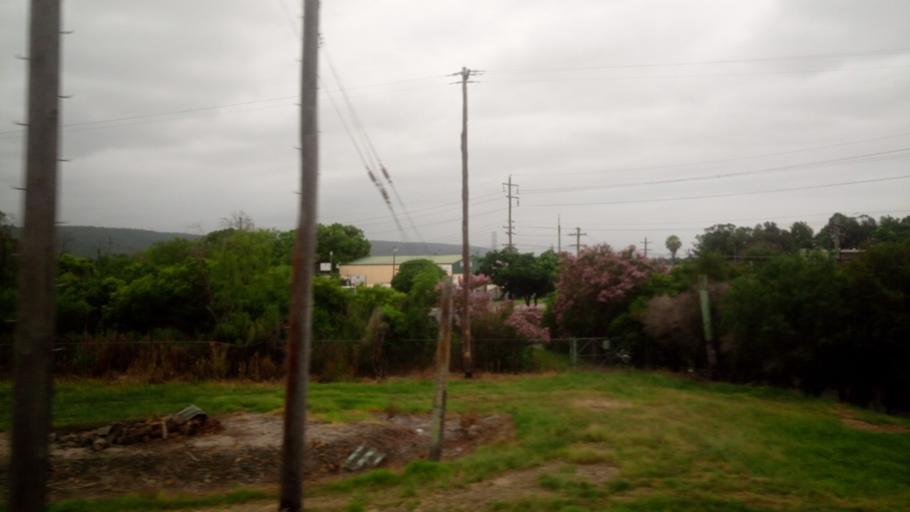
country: AU
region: New South Wales
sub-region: Penrith Municipality
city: Emu Heights
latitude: -33.7459
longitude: 150.6705
